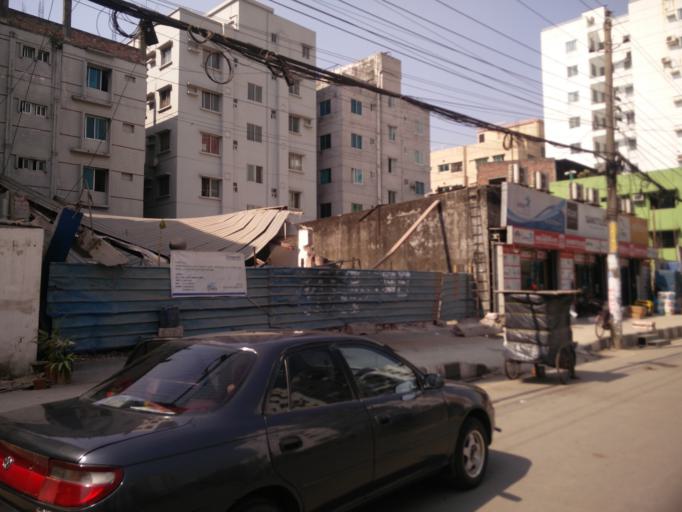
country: BD
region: Dhaka
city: Tungi
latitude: 23.8707
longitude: 90.3909
